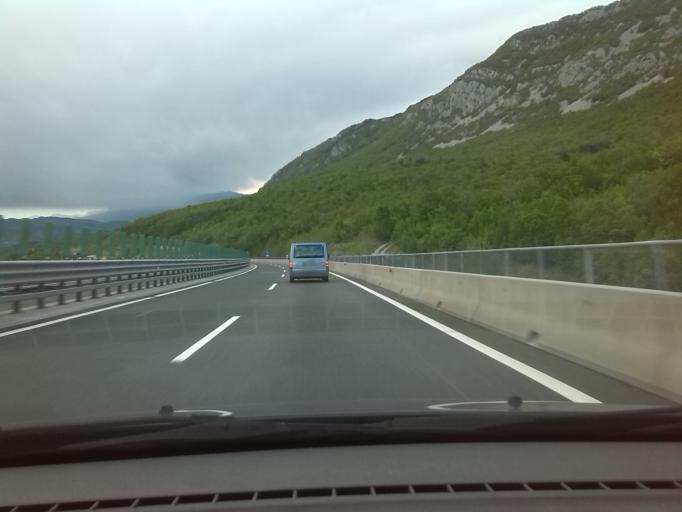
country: SI
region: Vipava
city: Vipava
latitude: 45.7760
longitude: 14.0212
